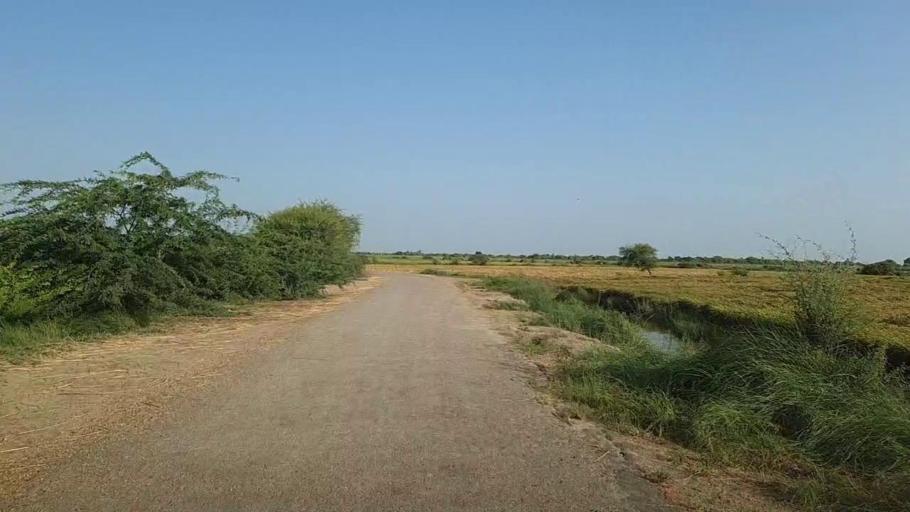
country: PK
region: Sindh
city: Kario
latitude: 24.7762
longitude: 68.6708
